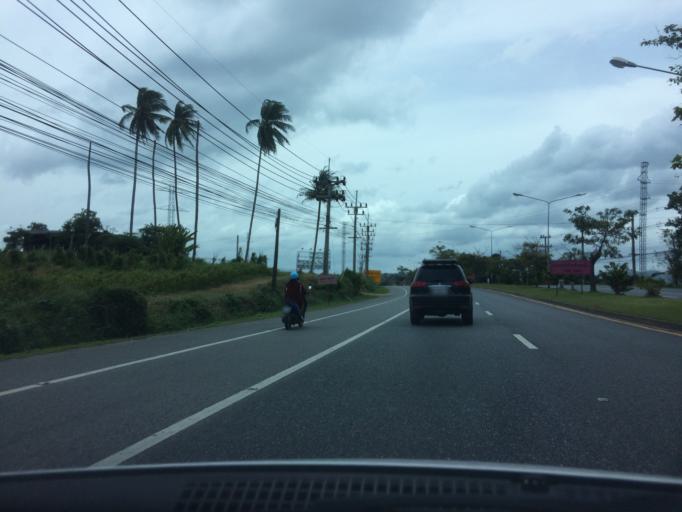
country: TH
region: Phuket
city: Thalang
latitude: 8.1324
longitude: 98.3403
